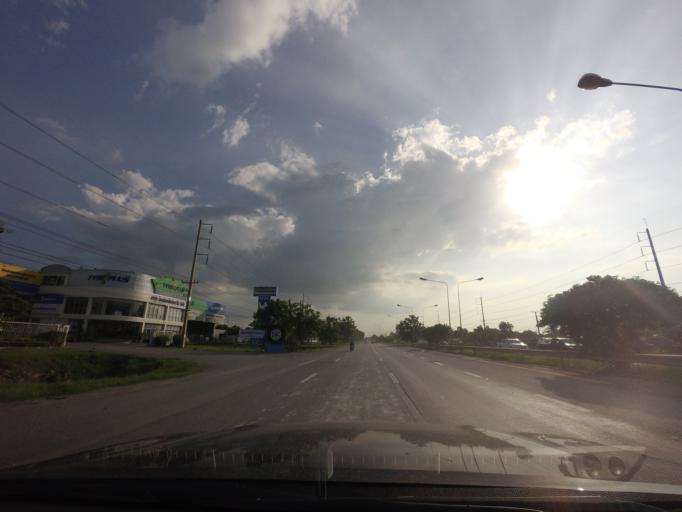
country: TH
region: Sara Buri
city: Saraburi
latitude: 14.5515
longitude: 100.8942
